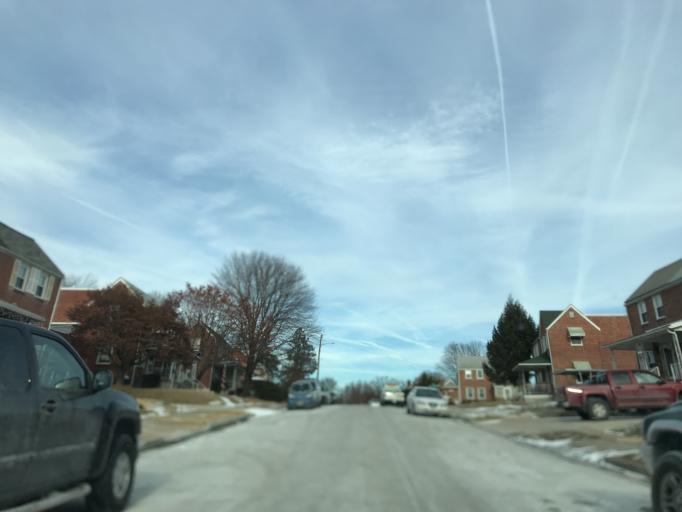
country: US
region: Maryland
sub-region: Baltimore County
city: Overlea
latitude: 39.3571
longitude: -76.5207
